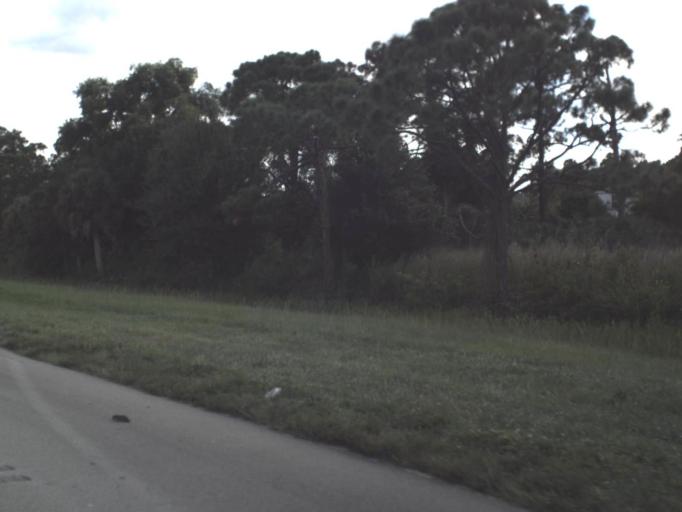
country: US
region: Florida
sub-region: Martin County
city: North River Shores
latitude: 27.2194
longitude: -80.3385
